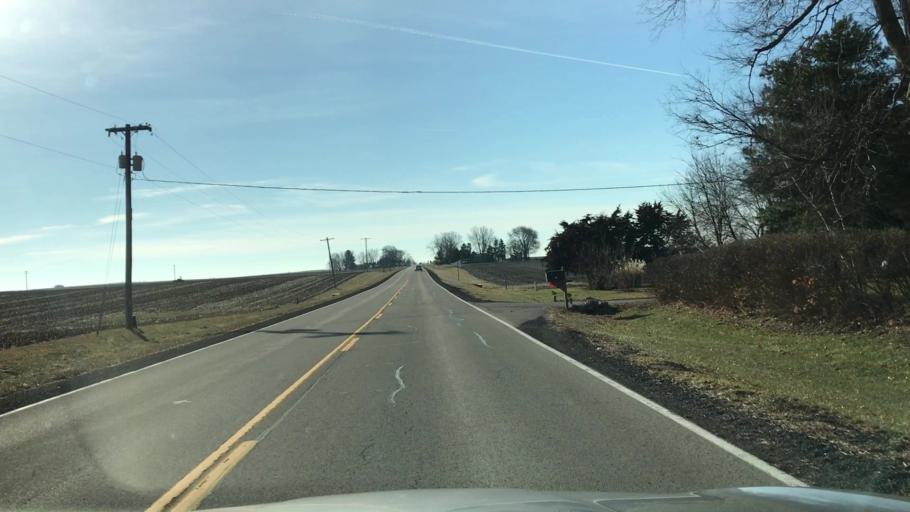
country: US
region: Illinois
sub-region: McLean County
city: Hudson
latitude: 40.6098
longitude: -88.9453
